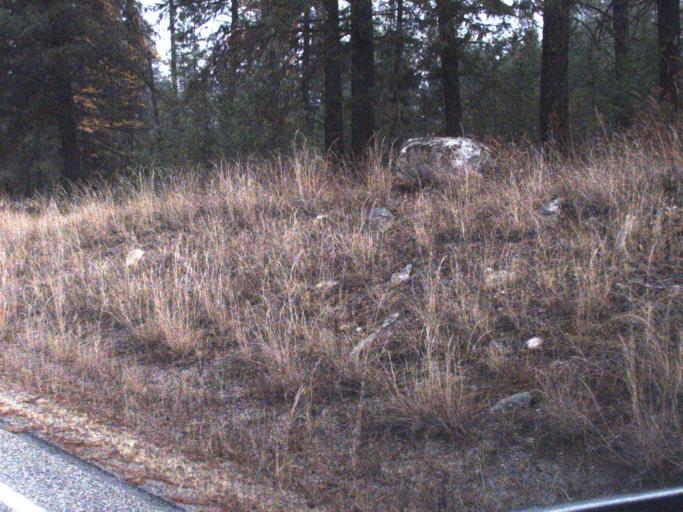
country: US
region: Washington
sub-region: Stevens County
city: Kettle Falls
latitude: 48.8363
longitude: -118.1861
